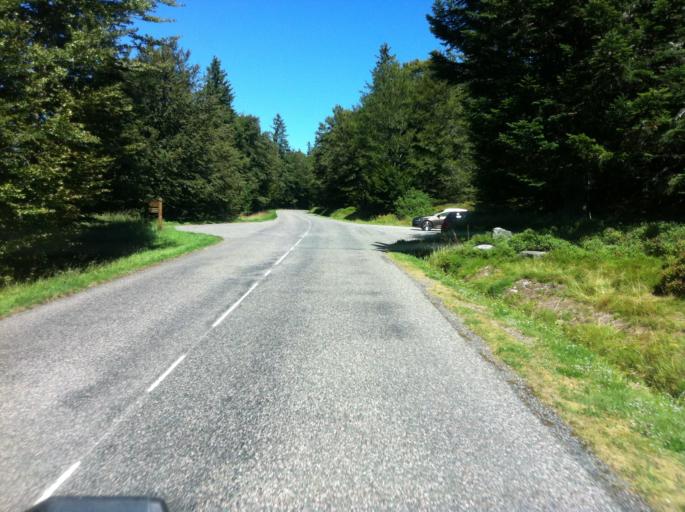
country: FR
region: Alsace
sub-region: Departement du Haut-Rhin
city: Soultzeren
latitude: 48.1280
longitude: 7.0728
